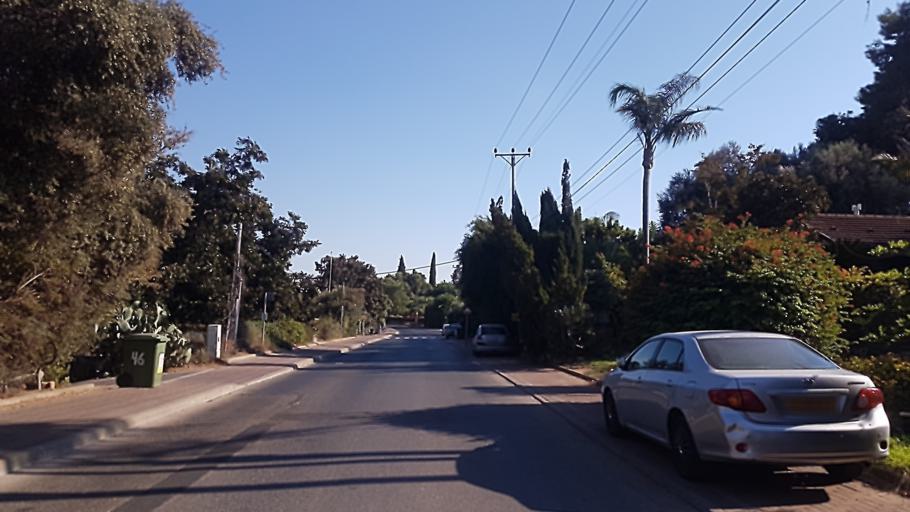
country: IL
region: Central District
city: Kfar Saba
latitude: 32.2059
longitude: 34.9047
